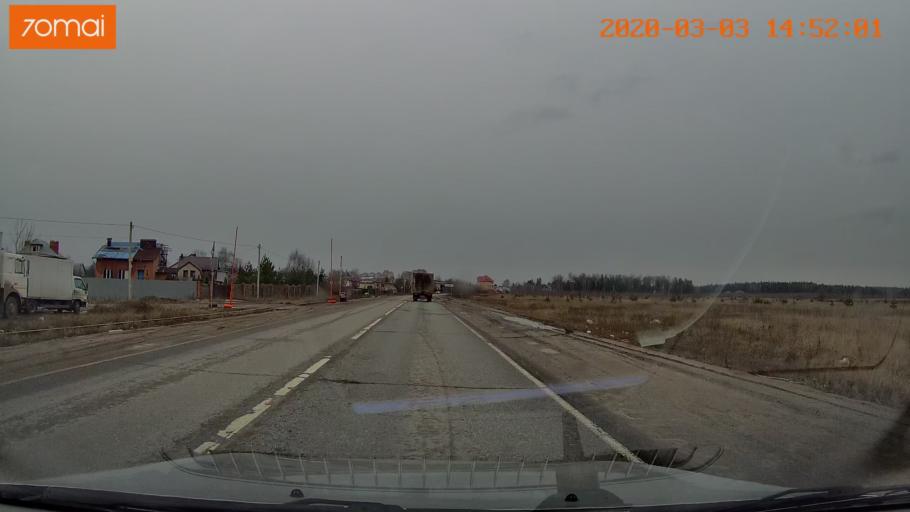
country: RU
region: Moskovskaya
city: Korenevo
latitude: 55.6673
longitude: 38.0202
